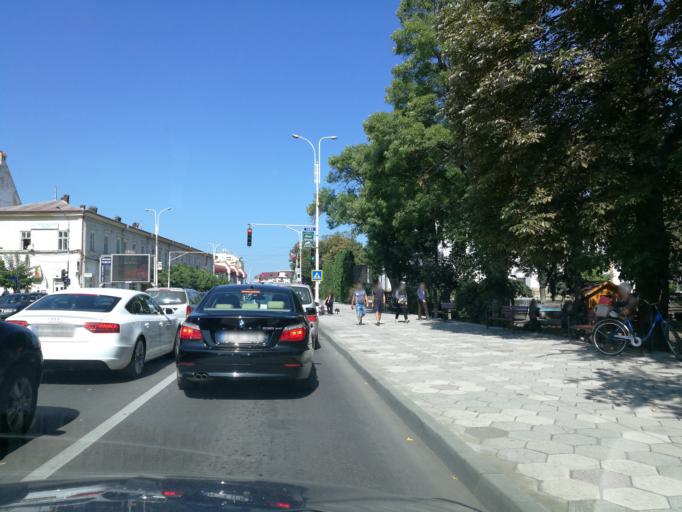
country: RO
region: Suceava
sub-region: Municipiul Suceava
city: Radauti
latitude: 47.8439
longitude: 25.9171
